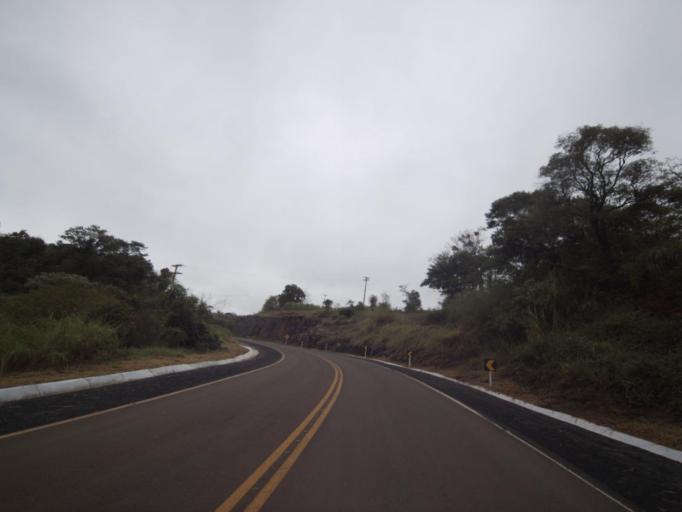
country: AR
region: Misiones
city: El Soberbio
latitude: -27.2889
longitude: -54.1759
